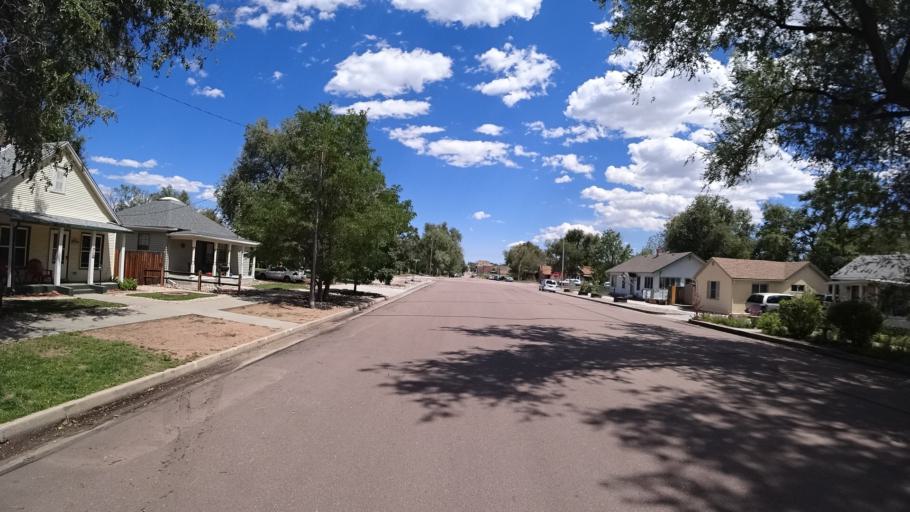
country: US
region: Colorado
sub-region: El Paso County
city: Colorado Springs
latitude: 38.8219
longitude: -104.8268
